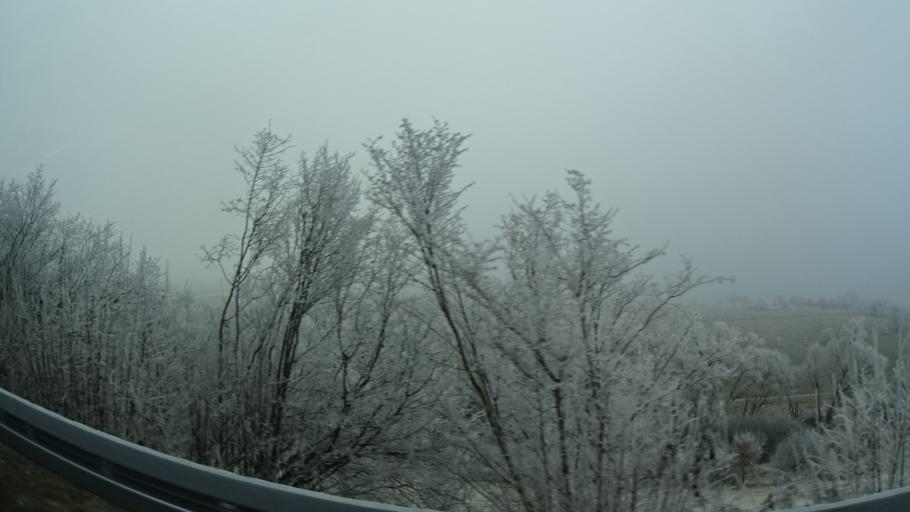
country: DE
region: Bavaria
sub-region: Regierungsbezirk Unterfranken
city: Johannesberg
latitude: 50.0510
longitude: 9.1295
